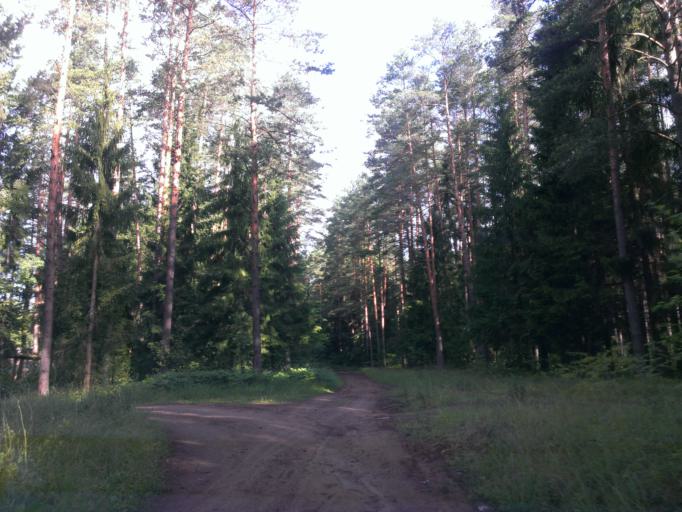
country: LV
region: Incukalns
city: Vangazi
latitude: 57.0984
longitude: 24.5409
